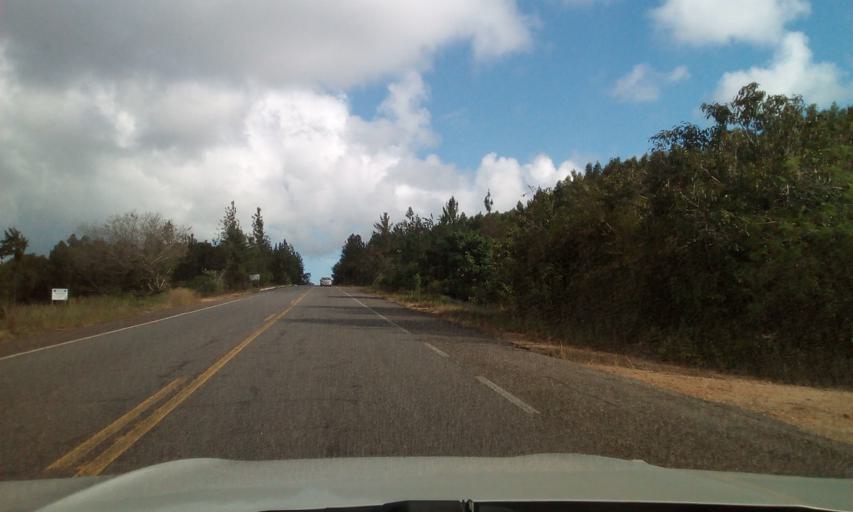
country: BR
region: Bahia
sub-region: Entre Rios
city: Entre Rios
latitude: -12.1364
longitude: -37.7916
